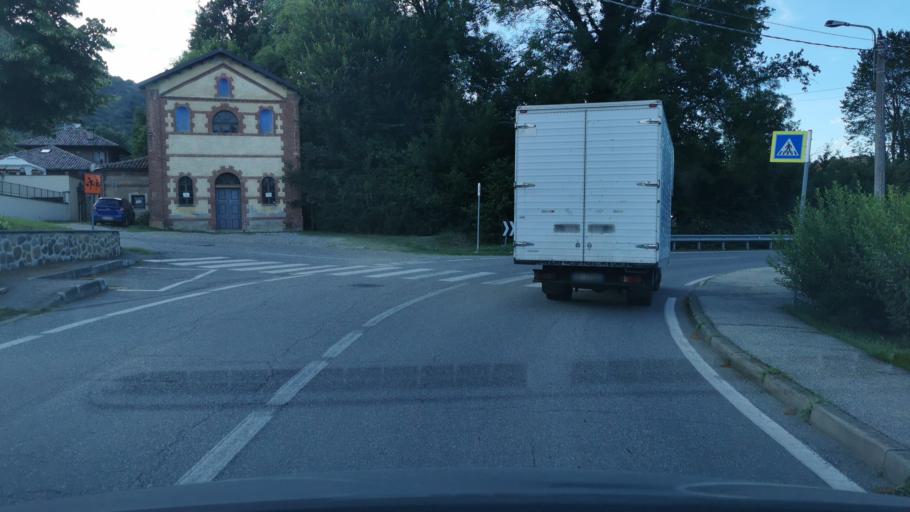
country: IT
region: Piedmont
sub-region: Provincia di Torino
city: La Cassa
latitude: 45.1782
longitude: 7.5171
